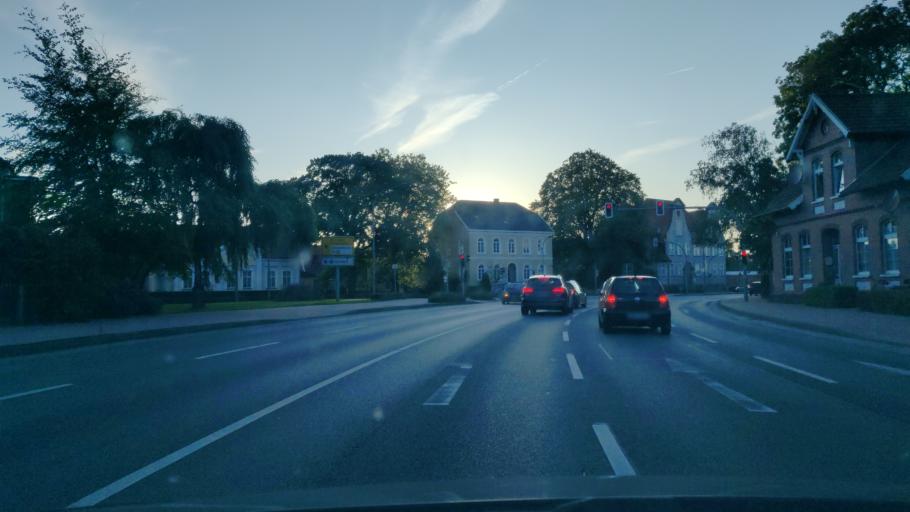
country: DE
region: Lower Saxony
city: Aurich
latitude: 53.4699
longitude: 7.4756
